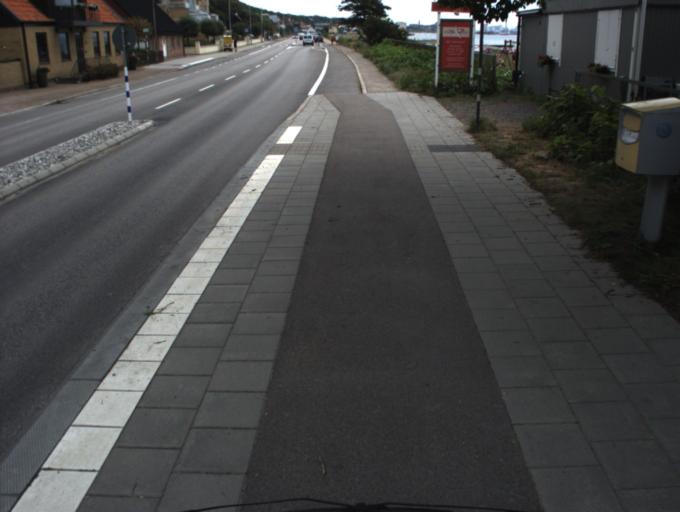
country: SE
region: Skane
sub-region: Helsingborg
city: Helsingborg
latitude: 56.0726
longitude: 12.6685
